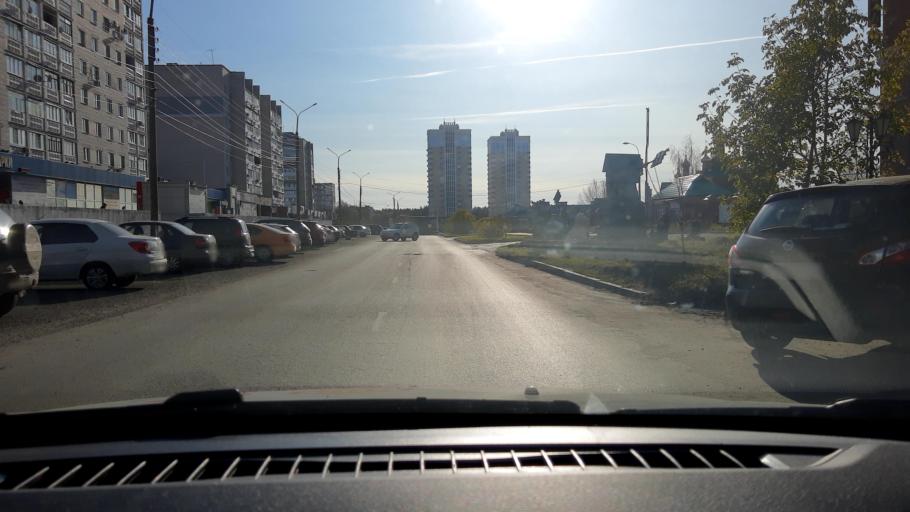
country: RU
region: Nizjnij Novgorod
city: Dzerzhinsk
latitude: 56.2309
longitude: 43.4163
